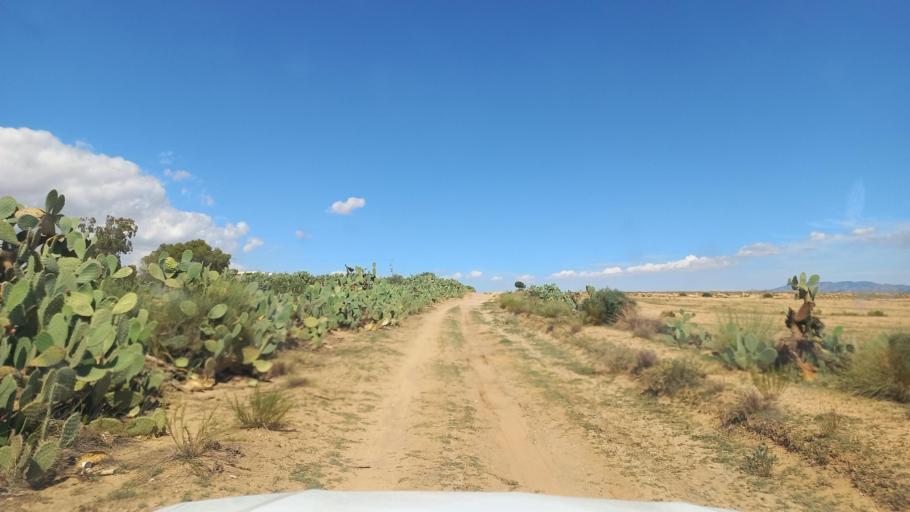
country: TN
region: Al Qasrayn
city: Sbiba
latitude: 35.3460
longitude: 9.0132
